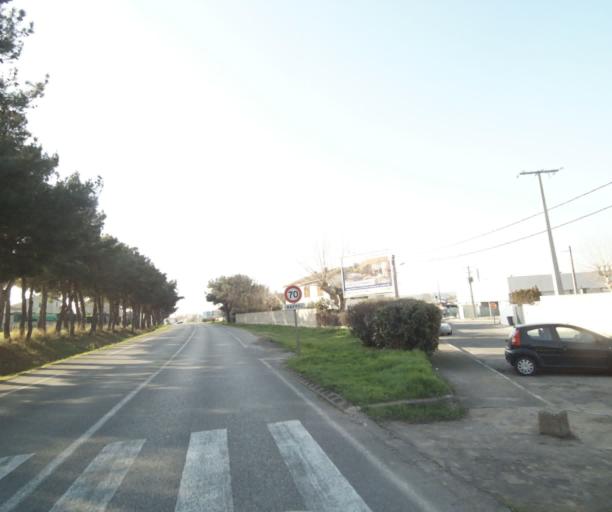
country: FR
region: Provence-Alpes-Cote d'Azur
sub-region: Departement des Bouches-du-Rhone
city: Les Pennes-Mirabeau
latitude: 43.4168
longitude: 5.2922
